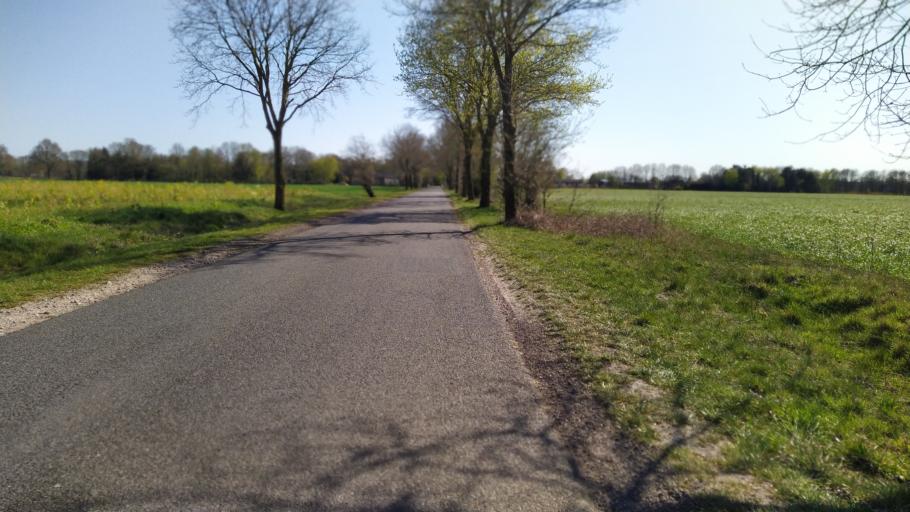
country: DE
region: Lower Saxony
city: Heeslingen
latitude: 53.3094
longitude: 9.3854
